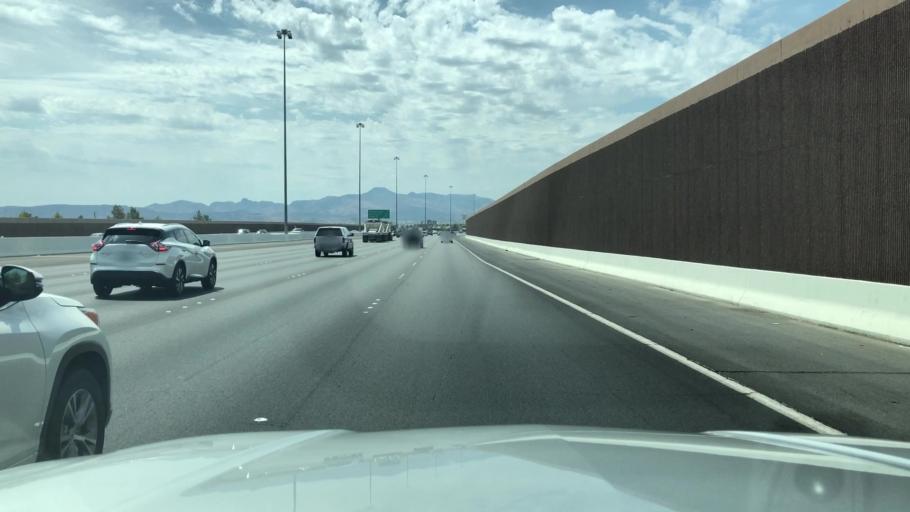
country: US
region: Nevada
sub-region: Clark County
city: Paradise
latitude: 36.0539
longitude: -115.1383
